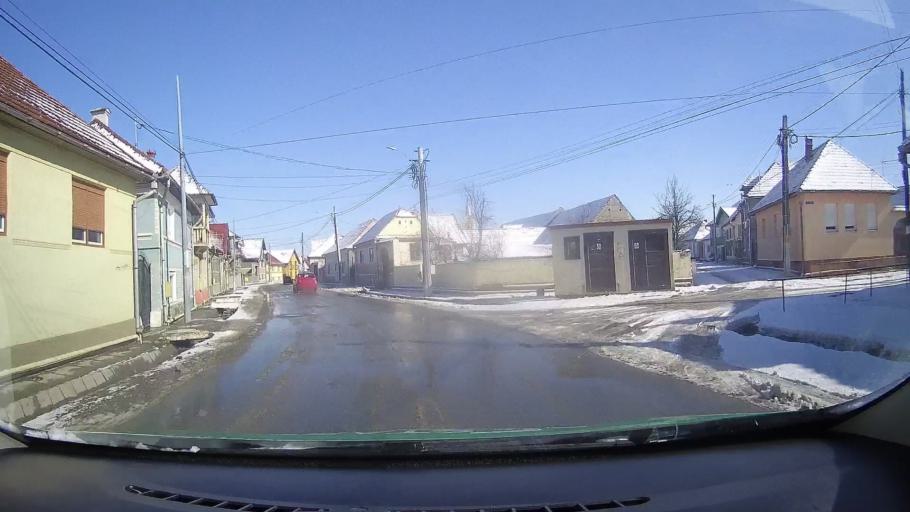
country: RO
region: Sibiu
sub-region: Comuna Racovita
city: Racovita
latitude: 45.6786
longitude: 24.3402
